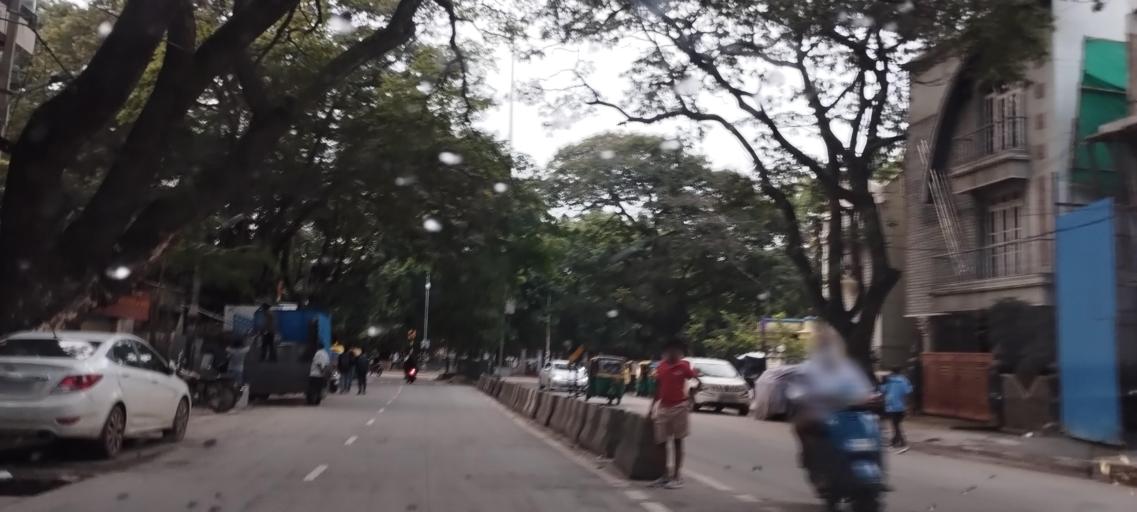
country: IN
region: Karnataka
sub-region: Bangalore Urban
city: Bangalore
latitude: 12.9512
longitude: 77.5768
